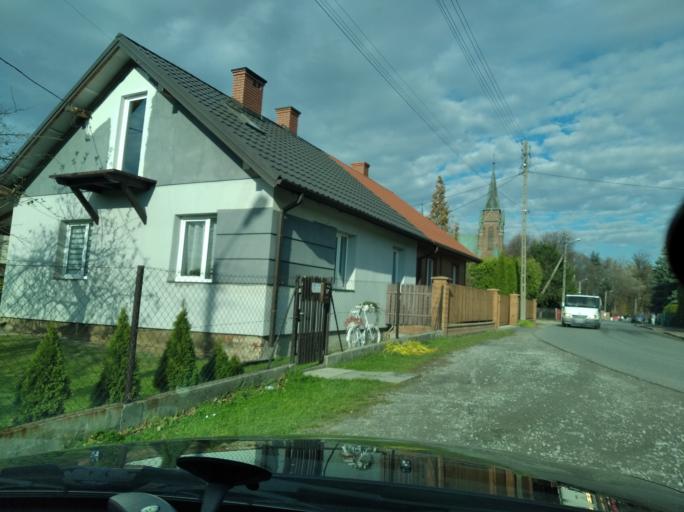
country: PL
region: Subcarpathian Voivodeship
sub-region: Powiat debicki
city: Brzeznica
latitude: 50.0641
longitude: 21.5255
